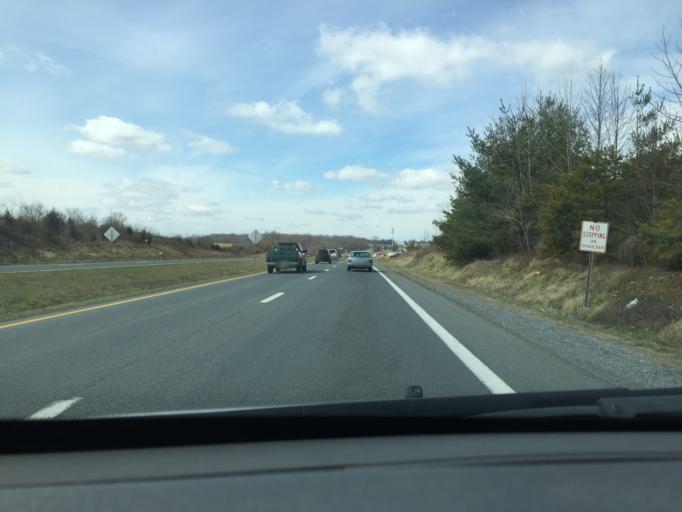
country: US
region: Virginia
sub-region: Campbell County
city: Timberlake
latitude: 37.3053
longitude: -79.2827
